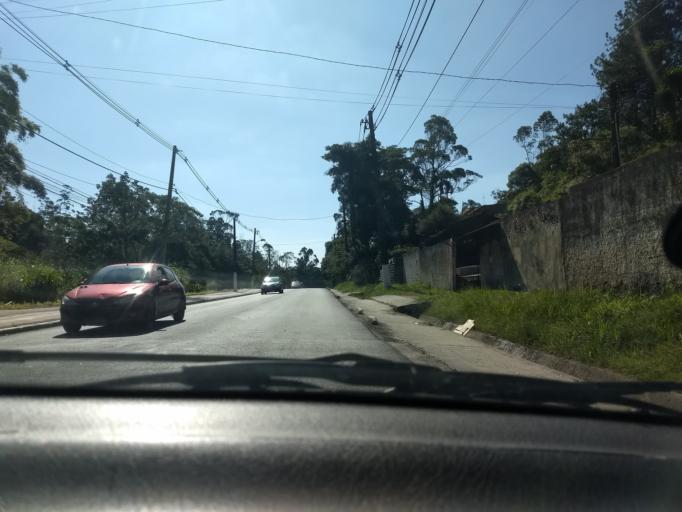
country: BR
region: Sao Paulo
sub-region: Embu-Guacu
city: Embu Guacu
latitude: -23.8339
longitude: -46.7305
